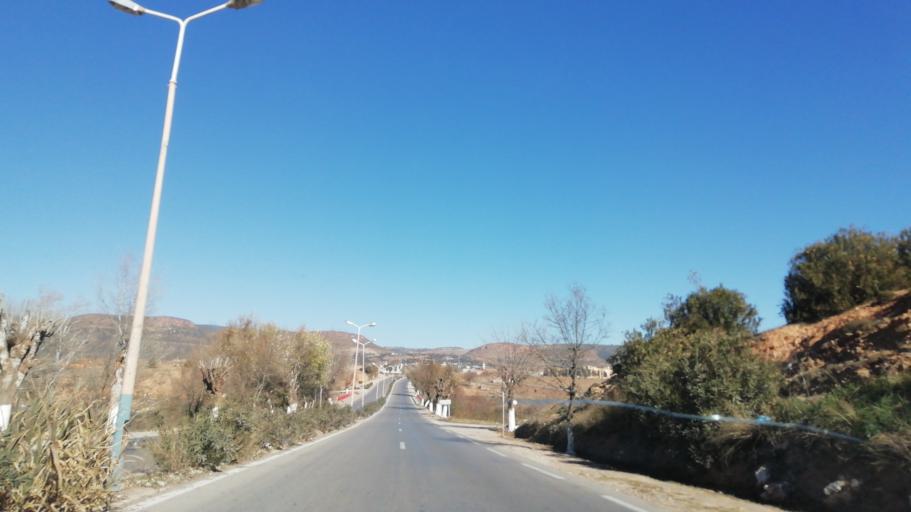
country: DZ
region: Tlemcen
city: Sebdou
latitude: 34.6552
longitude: -1.3252
